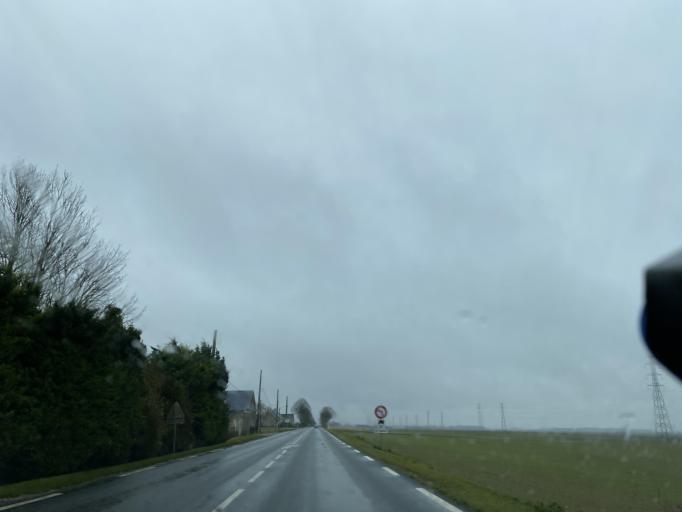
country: FR
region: Centre
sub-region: Departement d'Eure-et-Loir
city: Baigneaux
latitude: 48.1451
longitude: 1.8472
